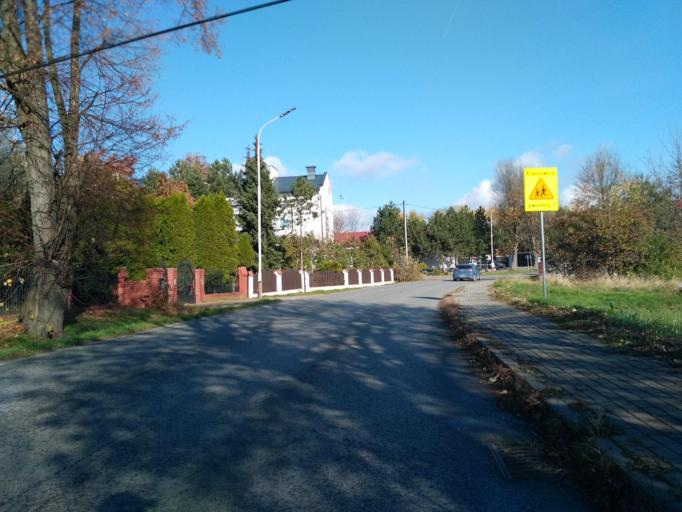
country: PL
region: Subcarpathian Voivodeship
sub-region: Powiat rzeszowski
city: Trzciana
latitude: 50.0705
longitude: 21.8353
